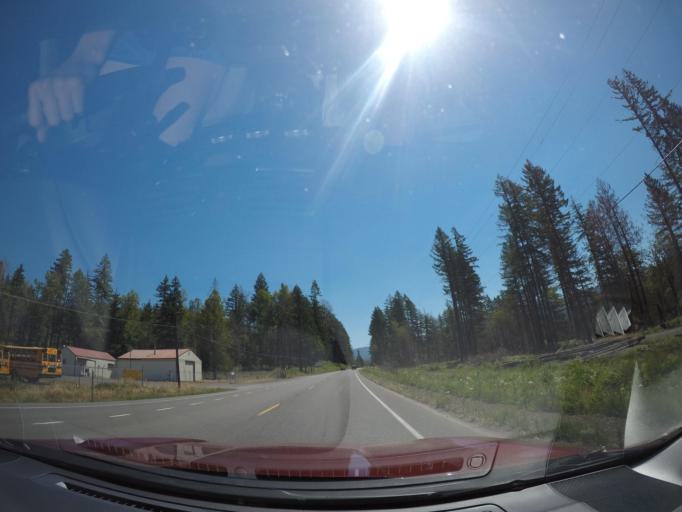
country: US
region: Oregon
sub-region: Linn County
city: Mill City
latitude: 44.7571
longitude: -122.4353
